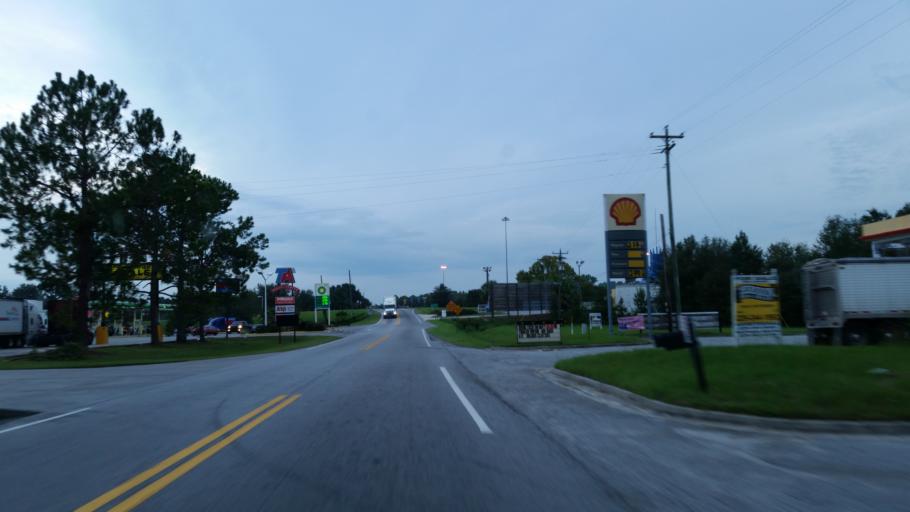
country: US
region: Georgia
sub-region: Echols County
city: Statenville
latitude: 30.6456
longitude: -83.1868
